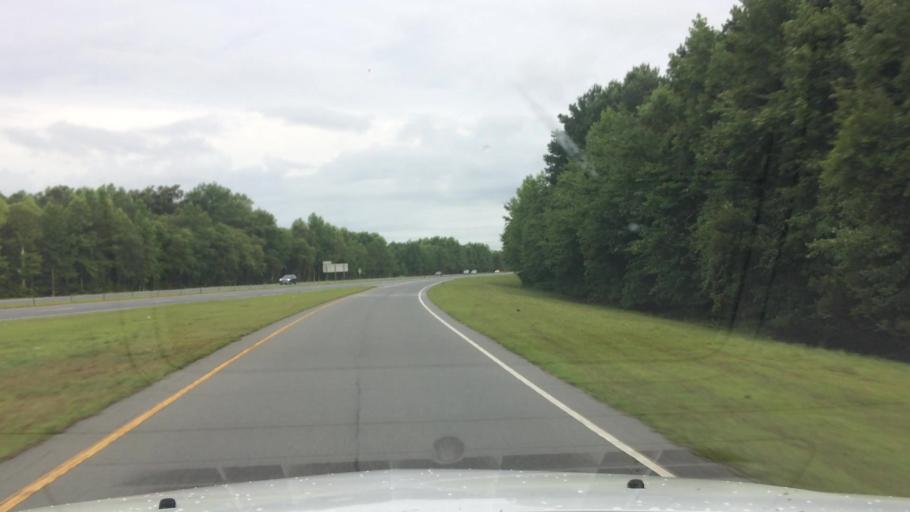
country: US
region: North Carolina
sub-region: Pitt County
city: Farmville
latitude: 35.6005
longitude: -77.5602
